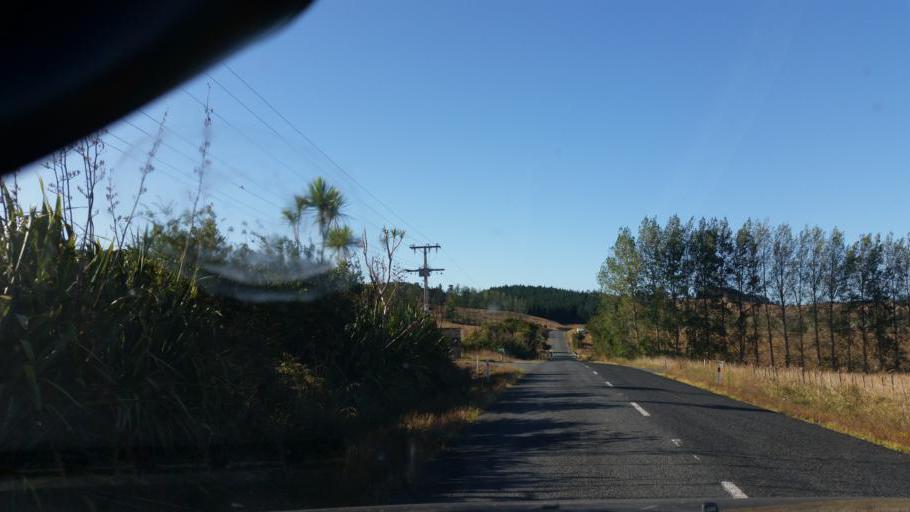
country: NZ
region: Northland
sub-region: Kaipara District
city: Dargaville
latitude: -36.0782
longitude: 174.1708
